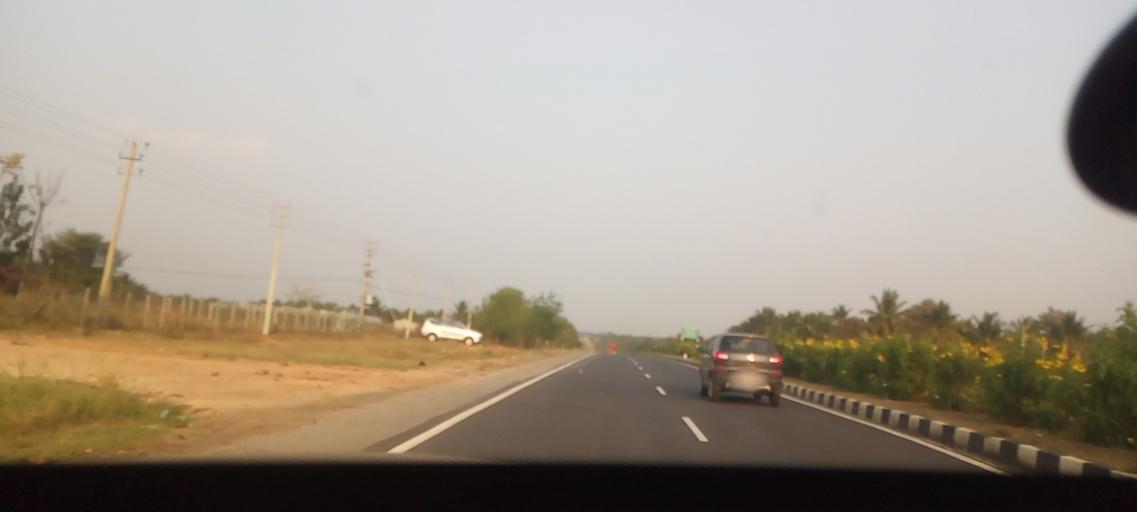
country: IN
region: Karnataka
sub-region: Mandya
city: Belluru
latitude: 12.9627
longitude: 76.6475
